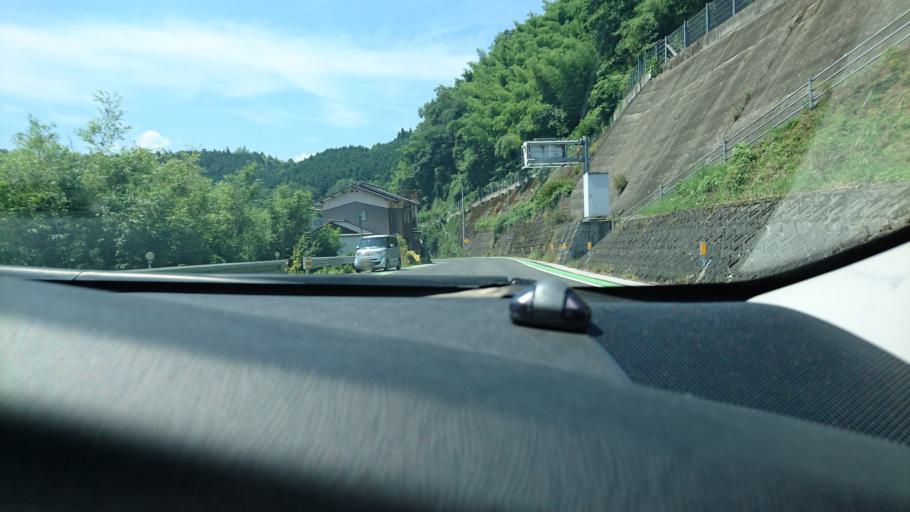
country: JP
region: Ehime
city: Ozu
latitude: 33.5014
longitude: 132.5463
